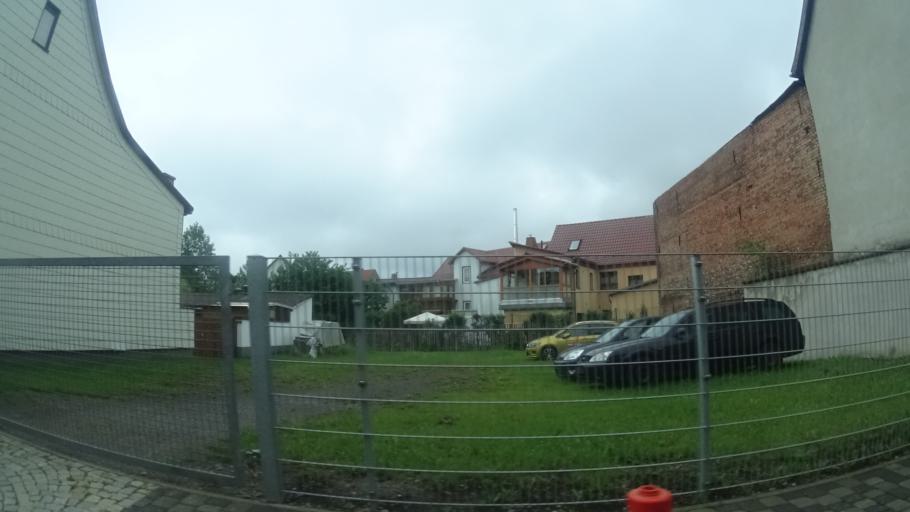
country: DE
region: Thuringia
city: Langewiesen
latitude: 50.6708
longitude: 10.9751
